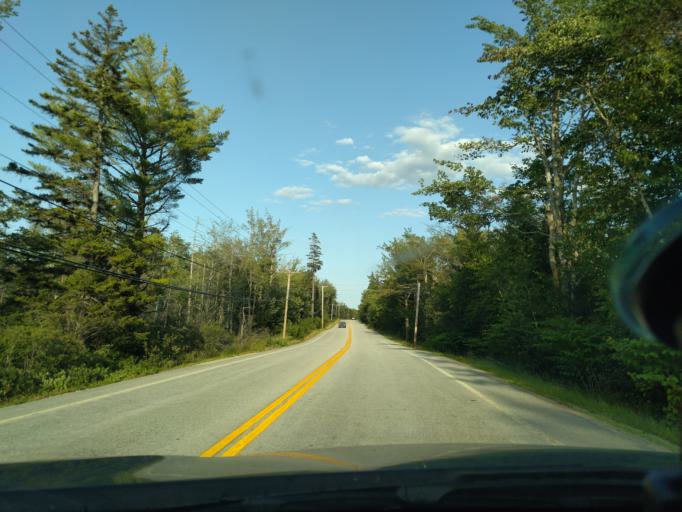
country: US
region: Maine
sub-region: Hancock County
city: Gouldsboro
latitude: 44.3934
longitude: -68.0631
